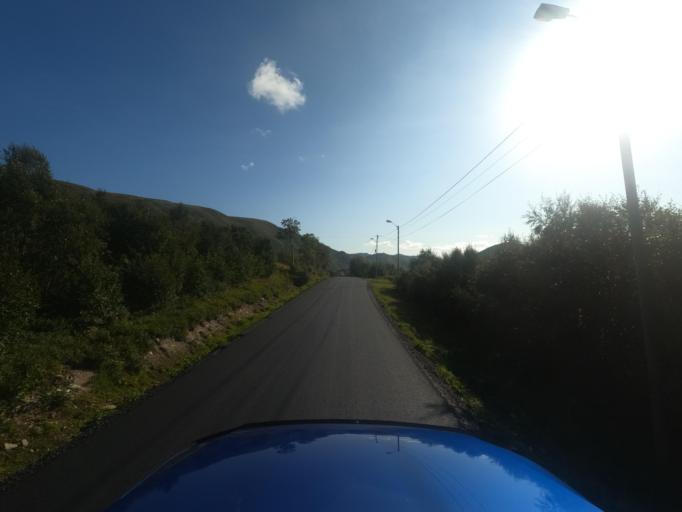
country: NO
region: Nordland
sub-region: Vestvagoy
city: Evjen
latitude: 68.2569
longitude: 13.8313
